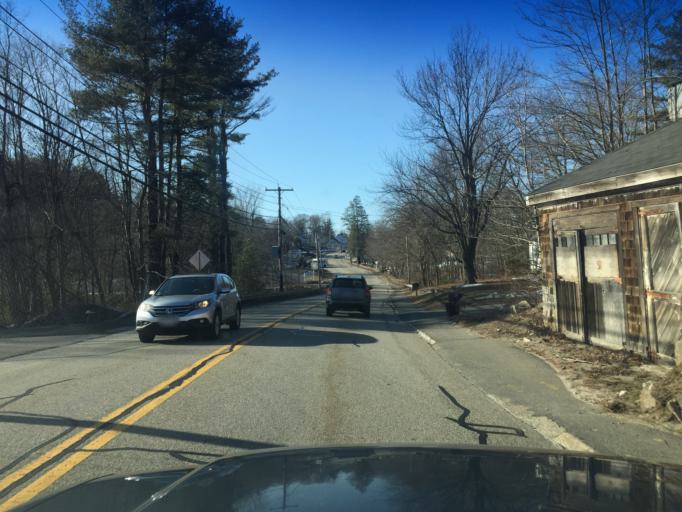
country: US
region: Massachusetts
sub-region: Norfolk County
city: Bellingham
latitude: 42.0830
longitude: -71.4690
